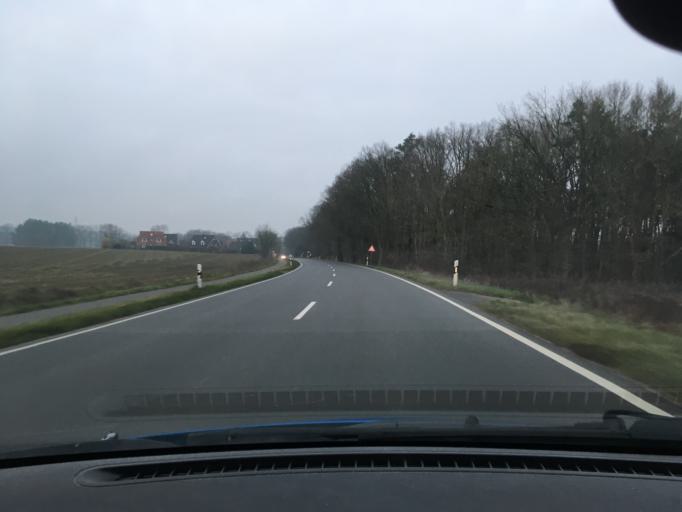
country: DE
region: Lower Saxony
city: Oldendorf
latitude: 53.1487
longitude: 10.2149
